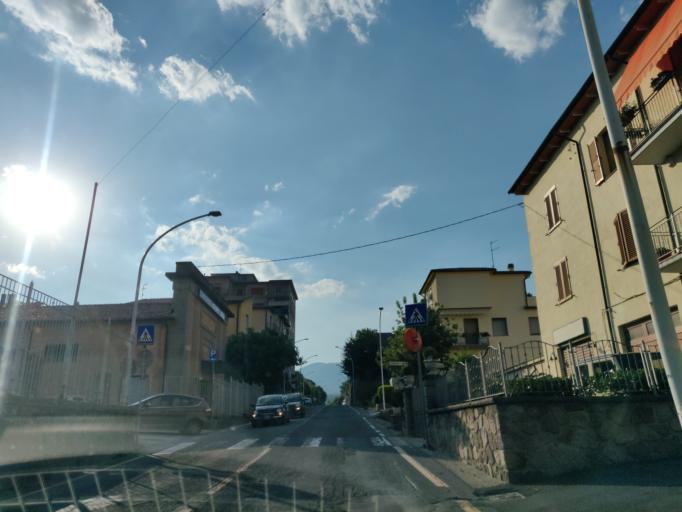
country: IT
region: Tuscany
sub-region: Provincia di Siena
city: Piancastagnaio
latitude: 42.8503
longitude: 11.6915
